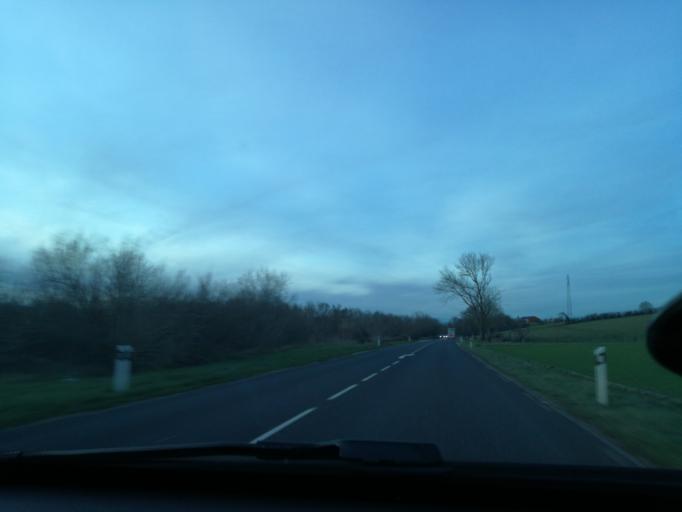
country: FR
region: Lorraine
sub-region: Departement de la Meuse
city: Fains-Veel
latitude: 48.8024
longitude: 5.1175
